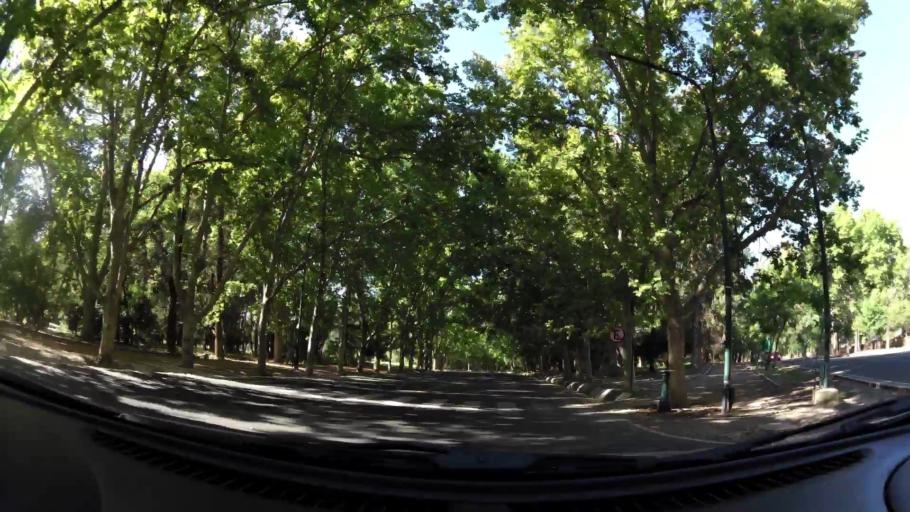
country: AR
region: Mendoza
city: Mendoza
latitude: -32.8859
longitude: -68.8734
